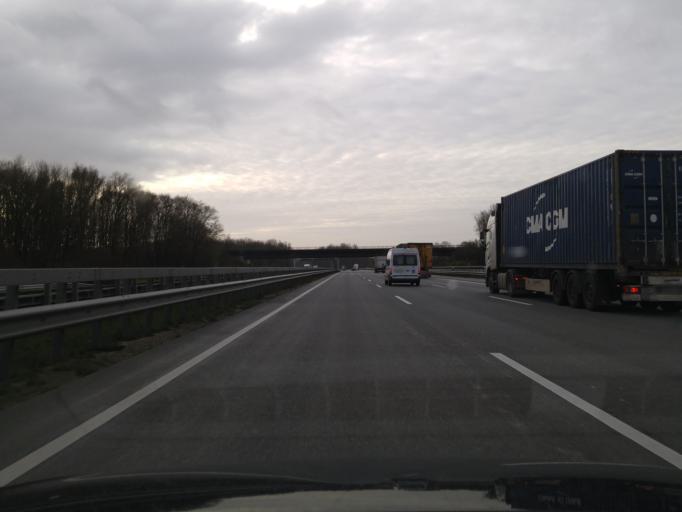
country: DE
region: Schleswig-Holstein
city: Hammoor
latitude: 53.7176
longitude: 10.3378
